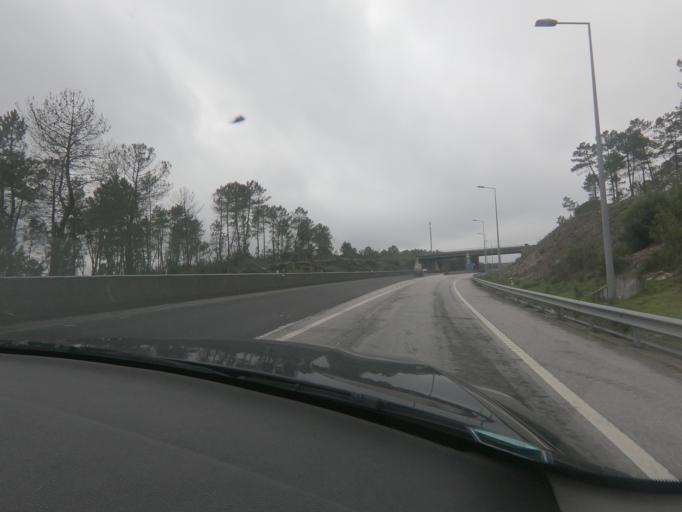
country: PT
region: Viseu
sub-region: Viseu
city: Abraveses
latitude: 40.6712
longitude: -7.9667
